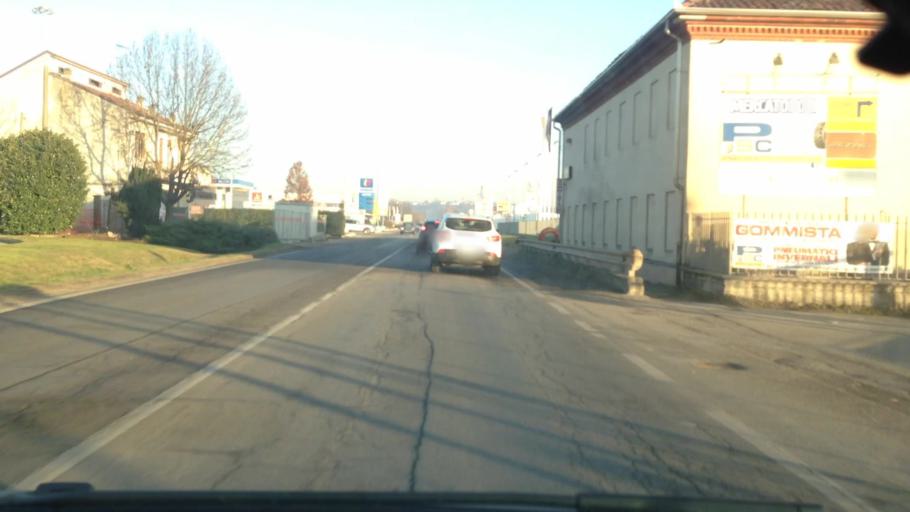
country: IT
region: Piedmont
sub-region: Provincia di Asti
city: Azzano d'Asti
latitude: 44.9061
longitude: 8.2600
